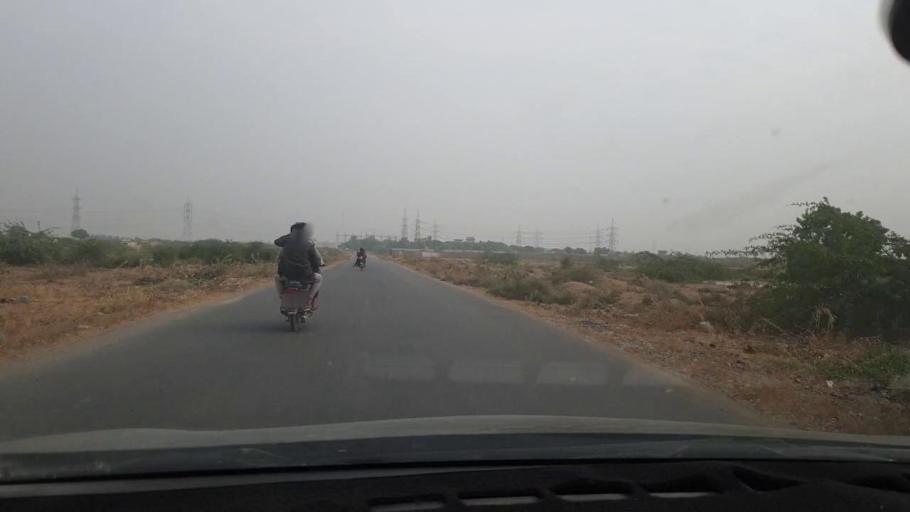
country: PK
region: Sindh
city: Malir Cantonment
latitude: 24.9130
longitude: 67.2756
